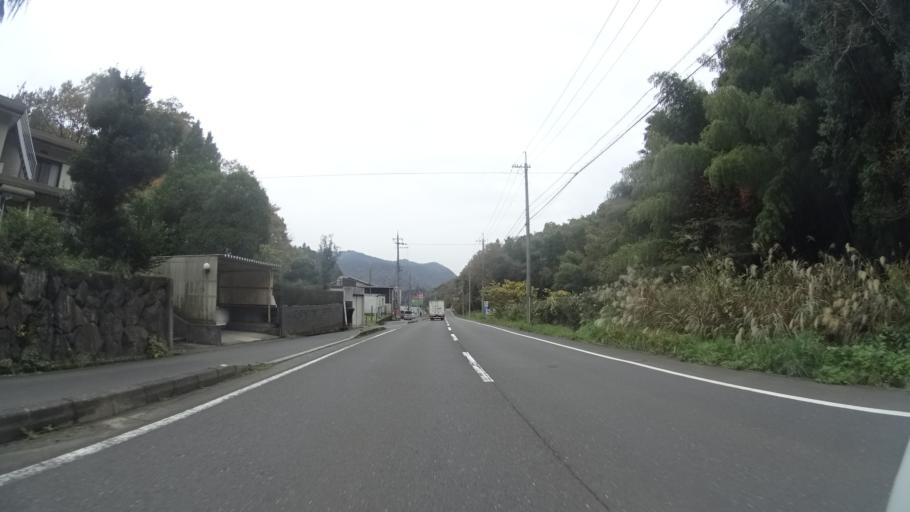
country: JP
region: Kyoto
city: Maizuru
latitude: 35.4697
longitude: 135.4239
